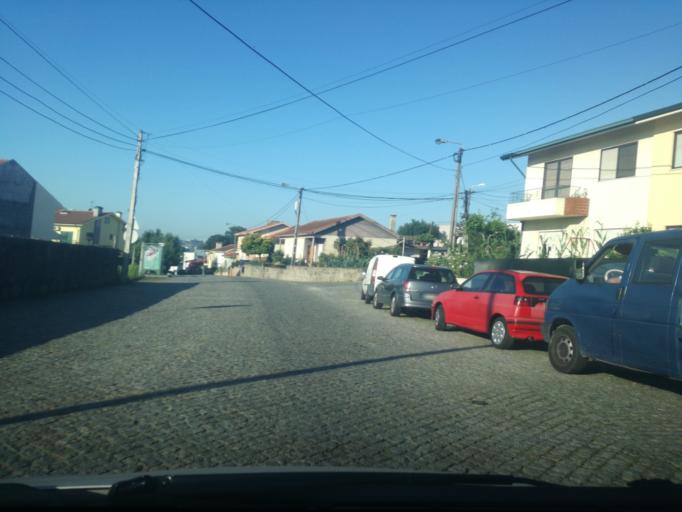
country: PT
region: Porto
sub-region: Maia
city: Milheiros
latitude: 41.2172
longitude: -8.5892
